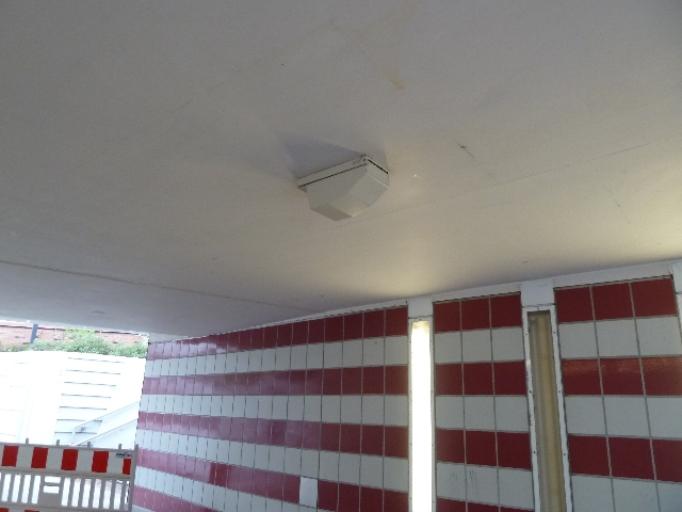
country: DE
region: Baden-Wuerttemberg
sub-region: Karlsruhe Region
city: Mosbach
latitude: 49.3524
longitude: 9.1435
